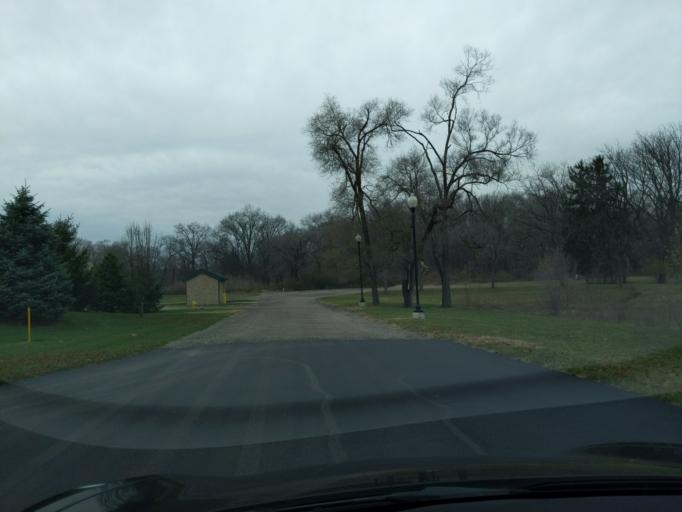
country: US
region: Indiana
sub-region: Saint Joseph County
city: Georgetown
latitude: 41.7332
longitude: -86.2666
